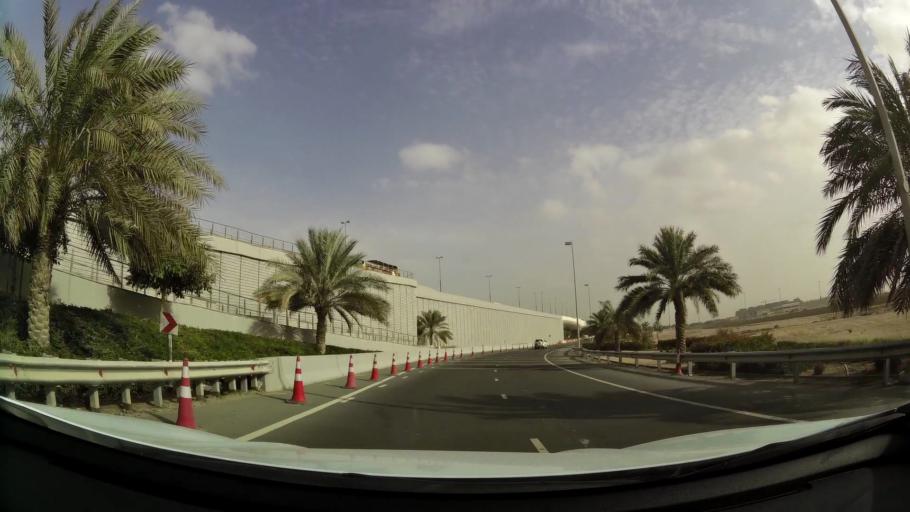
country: AE
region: Abu Dhabi
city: Abu Dhabi
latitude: 24.4484
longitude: 54.6165
